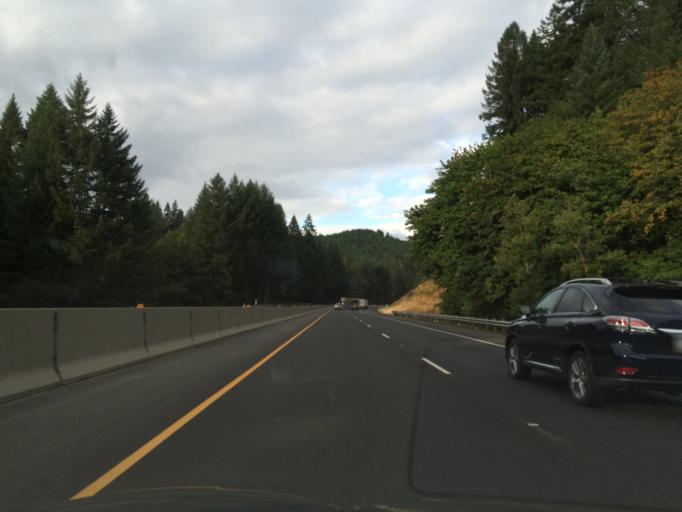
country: US
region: Oregon
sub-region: Lane County
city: Cottage Grove
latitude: 43.7482
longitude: -123.1772
